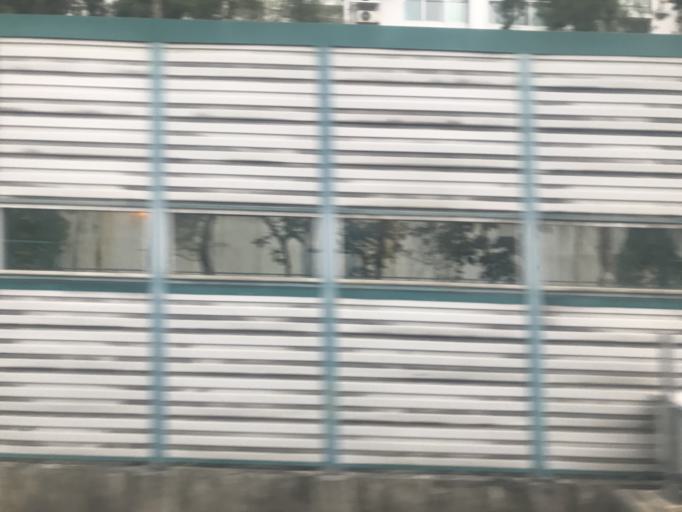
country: HK
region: Kowloon City
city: Kowloon
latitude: 22.3322
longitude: 114.1767
